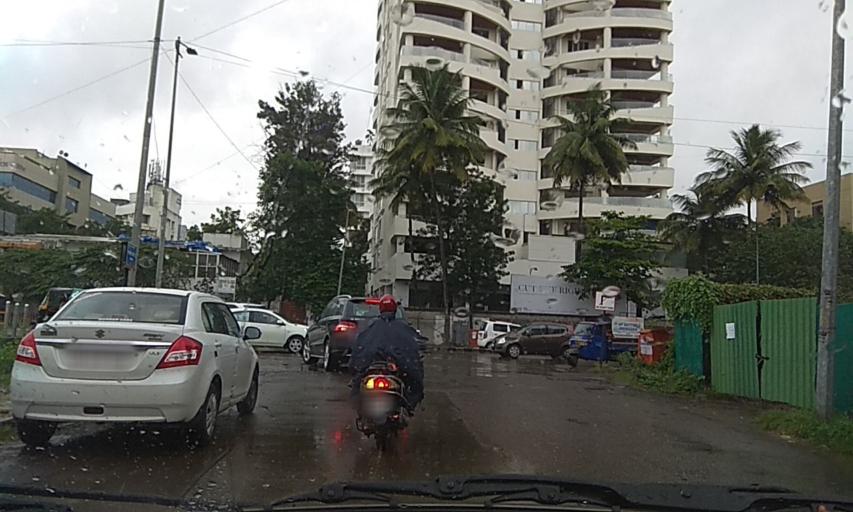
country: IN
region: Maharashtra
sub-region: Pune Division
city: Khadki
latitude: 18.5553
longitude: 73.7994
